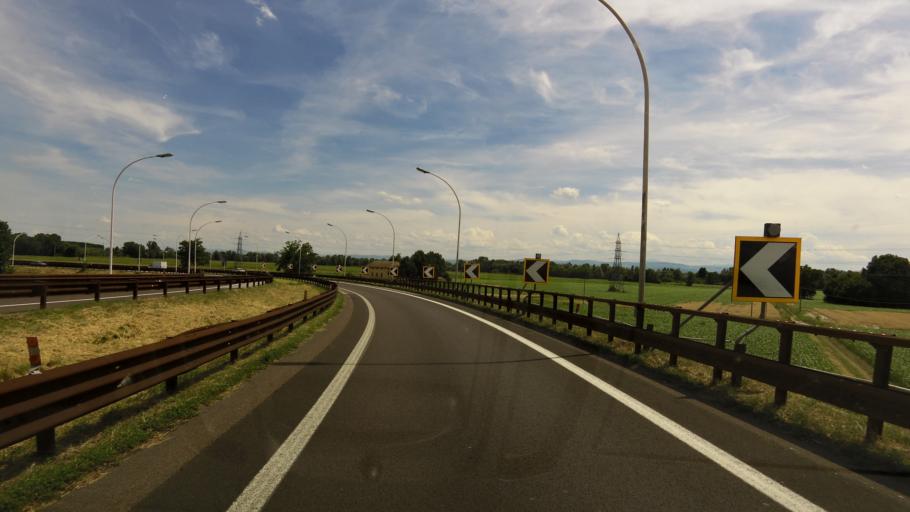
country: IT
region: Emilia-Romagna
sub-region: Provincia di Modena
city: Campogalliano
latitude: 44.6669
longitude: 10.8420
